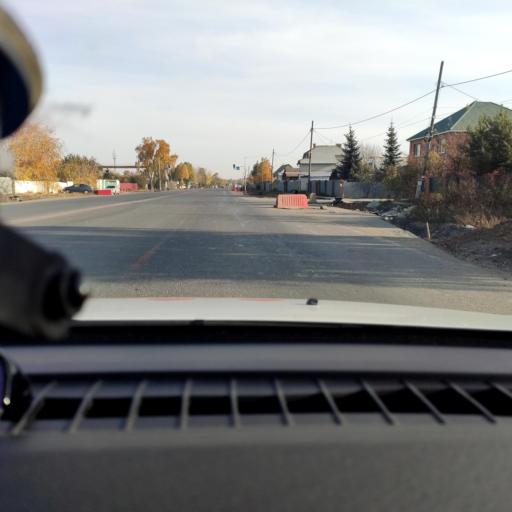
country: RU
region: Samara
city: Samara
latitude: 53.1291
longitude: 50.0922
